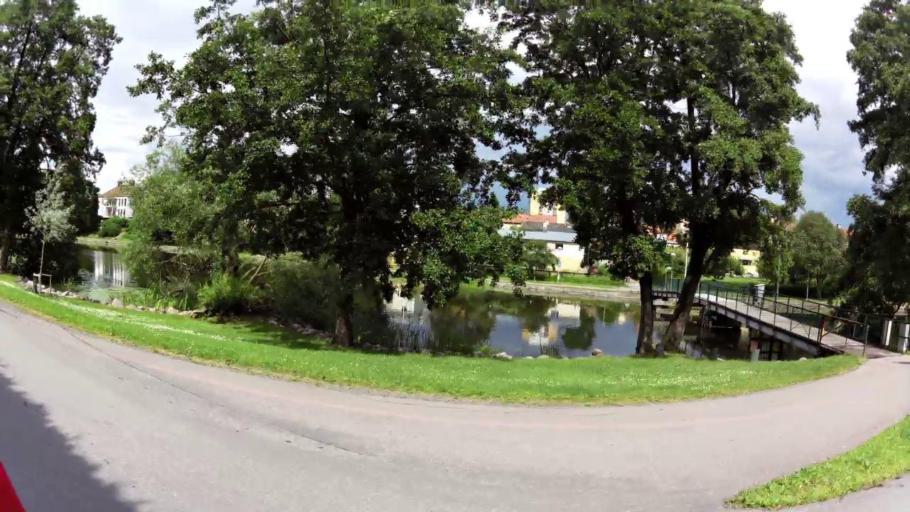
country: SE
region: OEstergoetland
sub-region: Linkopings Kommun
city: Linkoping
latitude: 58.4037
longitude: 15.6402
